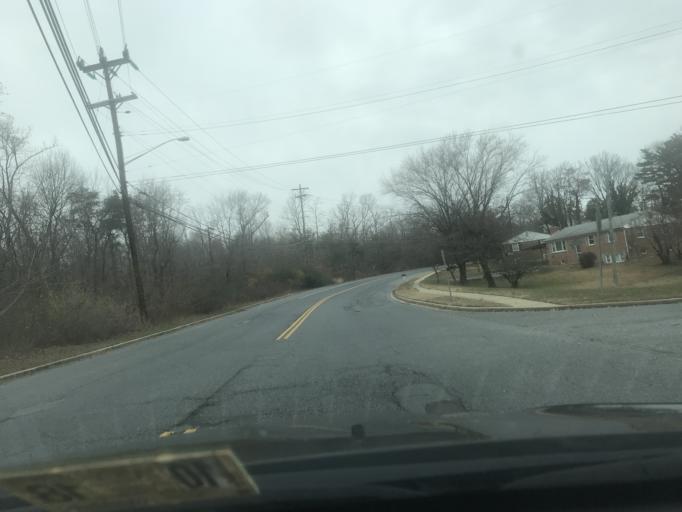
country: US
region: Maryland
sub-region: Prince George's County
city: Friendly
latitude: 38.7798
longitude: -76.9633
